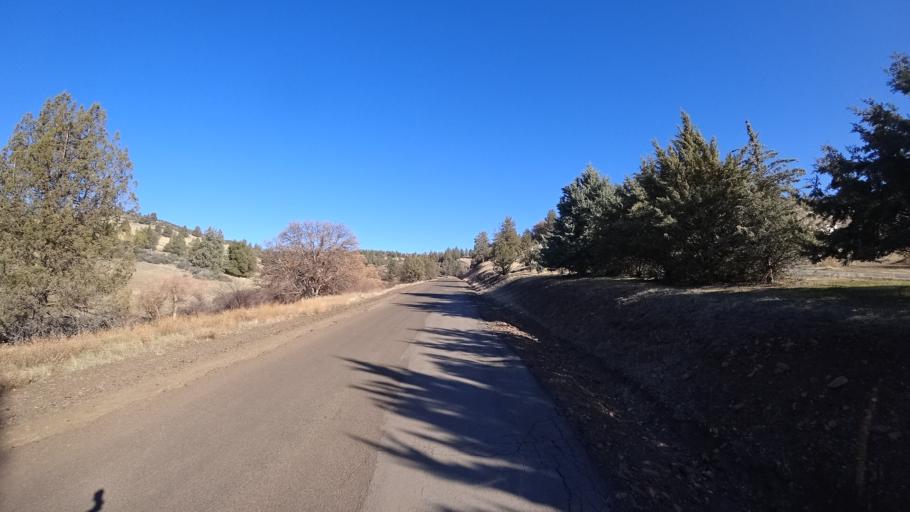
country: US
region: California
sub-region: Siskiyou County
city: Montague
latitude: 41.8964
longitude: -122.4243
